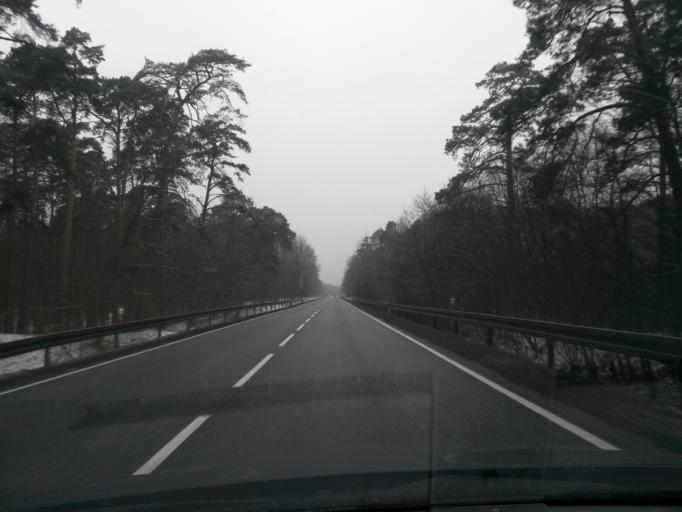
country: PL
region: Kujawsko-Pomorskie
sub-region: Powiat torunski
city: Wielka Nieszawka
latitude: 52.9811
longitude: 18.4953
